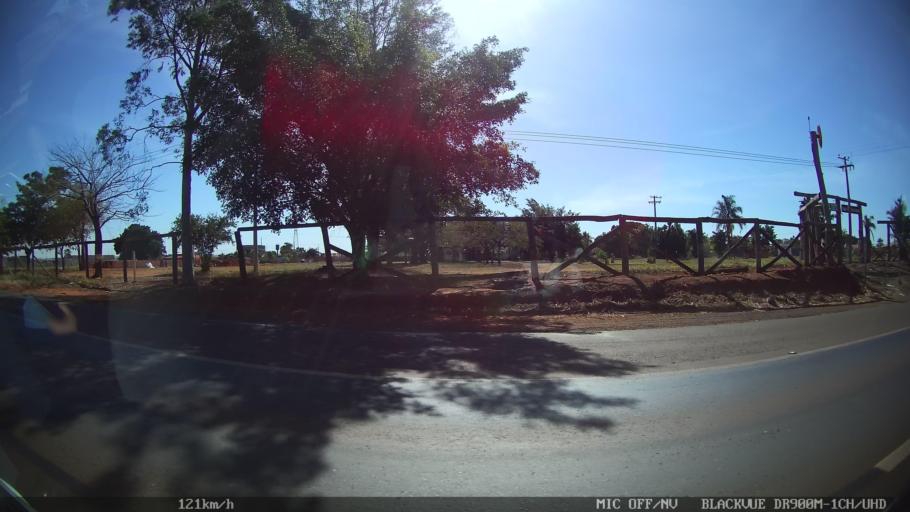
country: BR
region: Sao Paulo
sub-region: Barretos
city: Barretos
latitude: -20.5415
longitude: -48.6168
